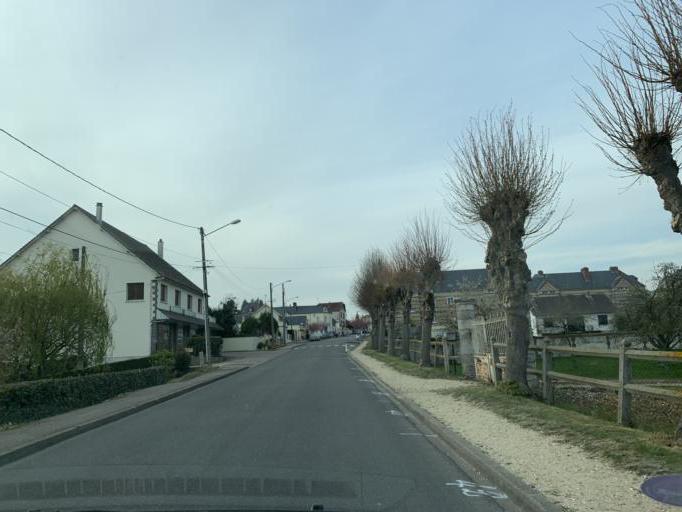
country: FR
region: Haute-Normandie
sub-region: Departement de la Seine-Maritime
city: La Mailleraye-sur-Seine
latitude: 49.4806
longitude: 0.7726
